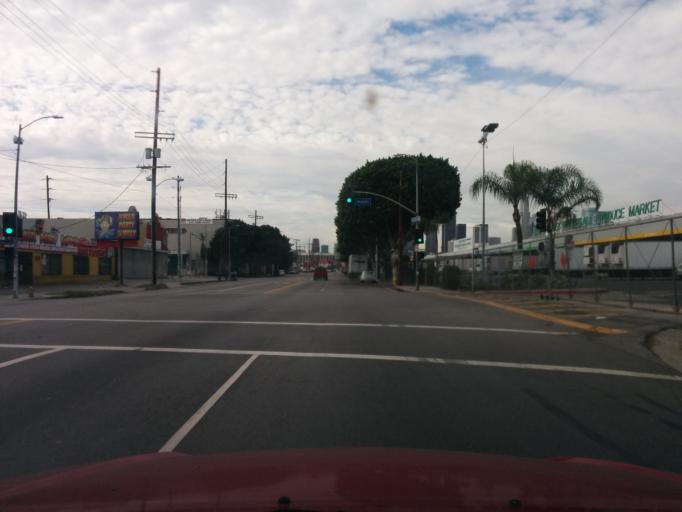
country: US
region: California
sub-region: Los Angeles County
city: Los Angeles
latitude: 34.0299
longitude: -118.2417
